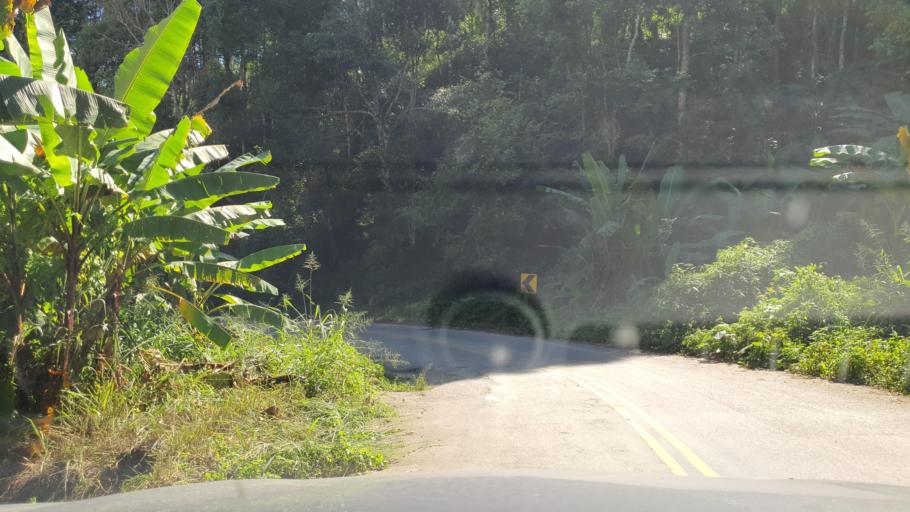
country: TH
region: Chiang Mai
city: Phrao
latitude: 19.3084
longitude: 99.3418
